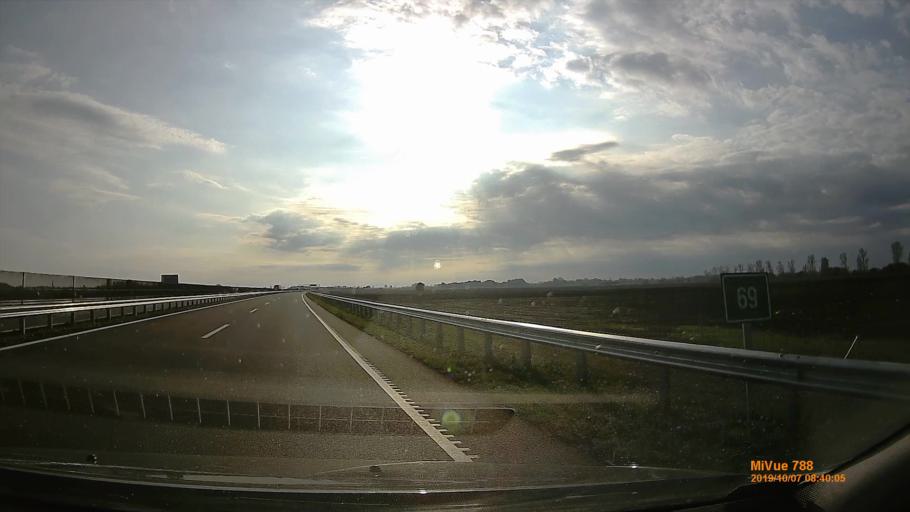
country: HU
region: Bekes
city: Bekesszentandras
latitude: 46.8253
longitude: 20.4908
